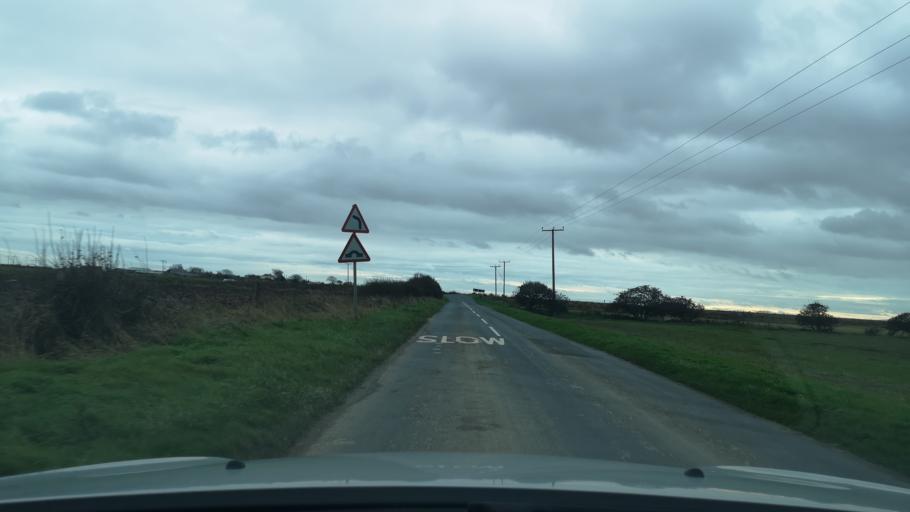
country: GB
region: England
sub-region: East Riding of Yorkshire
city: Easington
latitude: 53.6306
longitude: 0.1228
